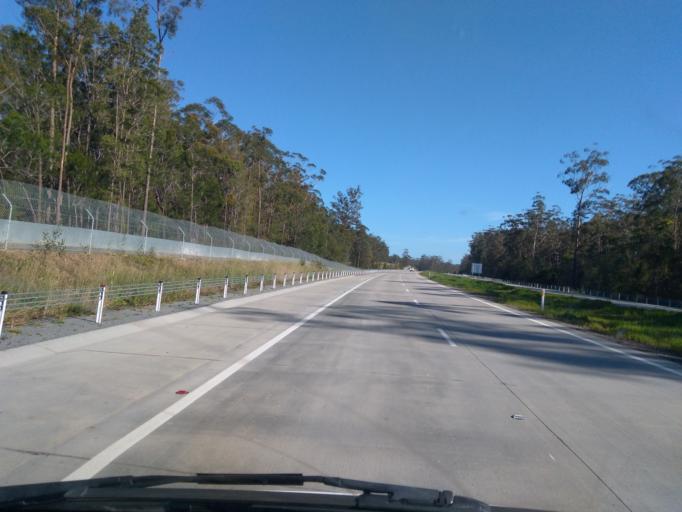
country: AU
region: New South Wales
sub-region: Port Macquarie-Hastings
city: North Shore
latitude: -31.3812
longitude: 152.8046
